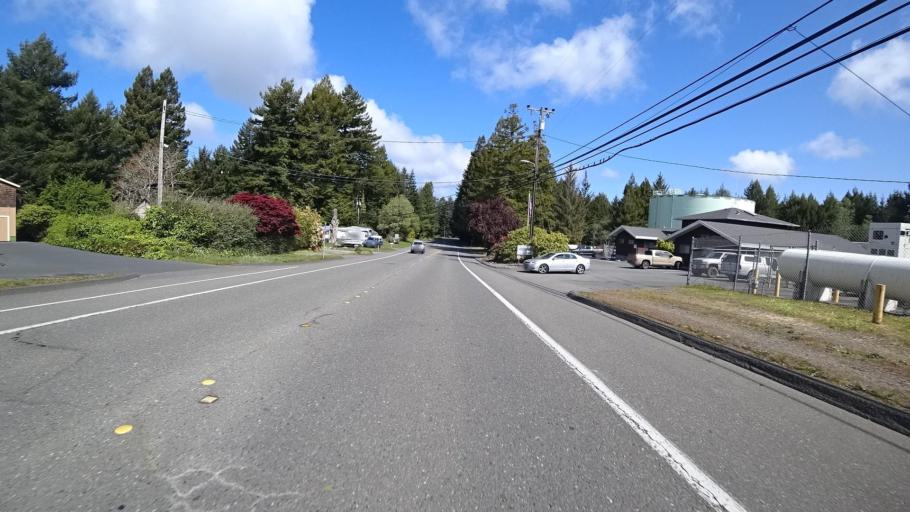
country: US
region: California
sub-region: Humboldt County
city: Cutten
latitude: 40.7532
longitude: -124.1457
